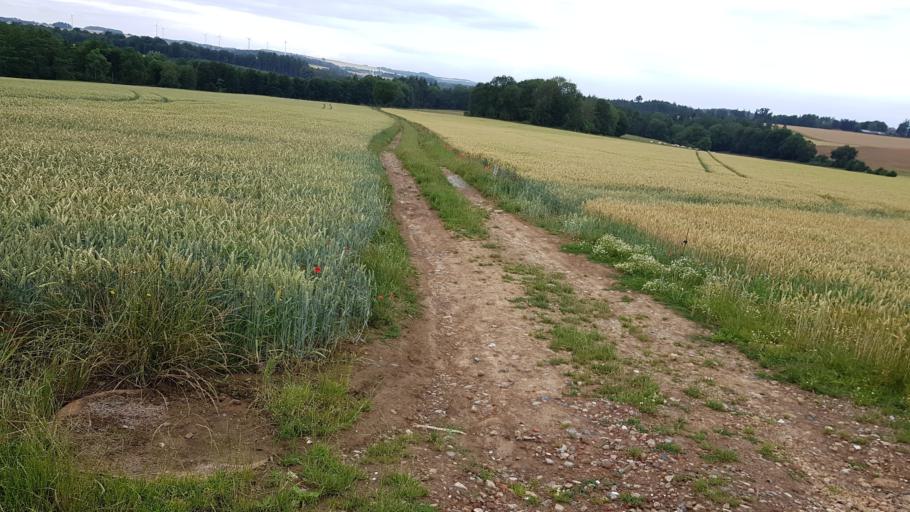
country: BE
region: Wallonia
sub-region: Province de Namur
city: Dinant
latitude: 50.2321
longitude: 4.9376
